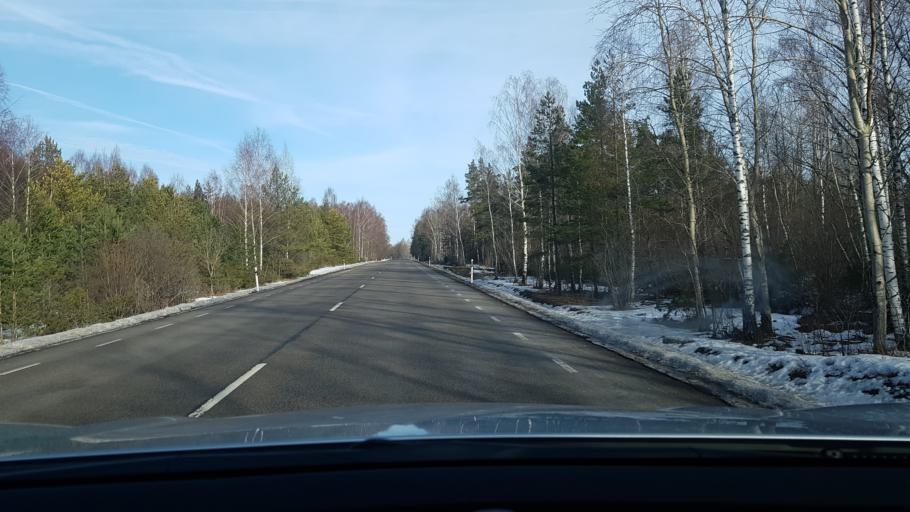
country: EE
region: Saare
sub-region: Orissaare vald
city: Orissaare
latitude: 58.5423
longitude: 23.0531
